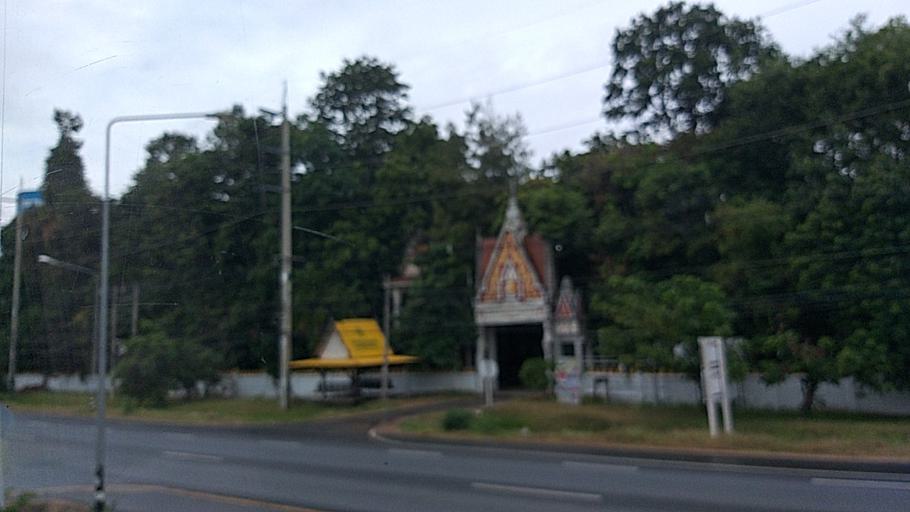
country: TH
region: Maha Sarakham
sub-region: Amphoe Borabue
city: Borabue
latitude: 16.0468
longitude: 103.1255
